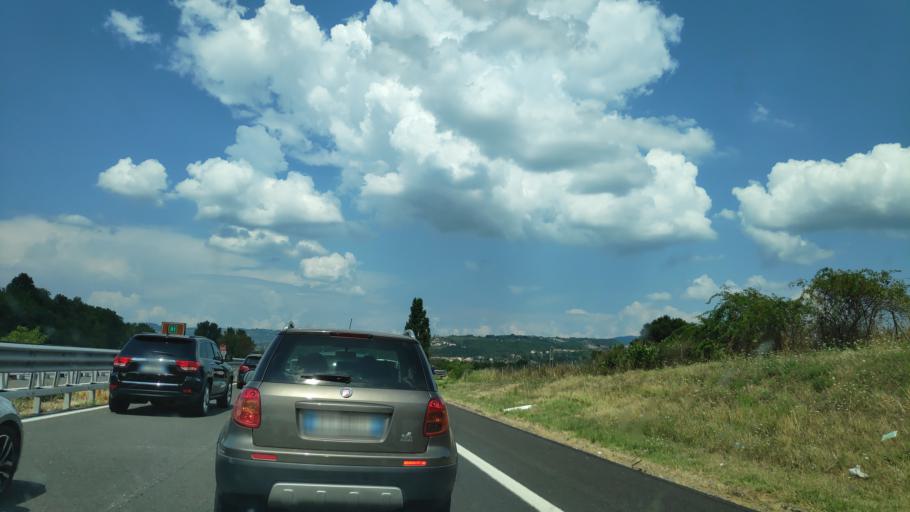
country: IT
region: Umbria
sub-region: Provincia di Terni
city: Fabro Scalo
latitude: 42.8563
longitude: 12.0381
